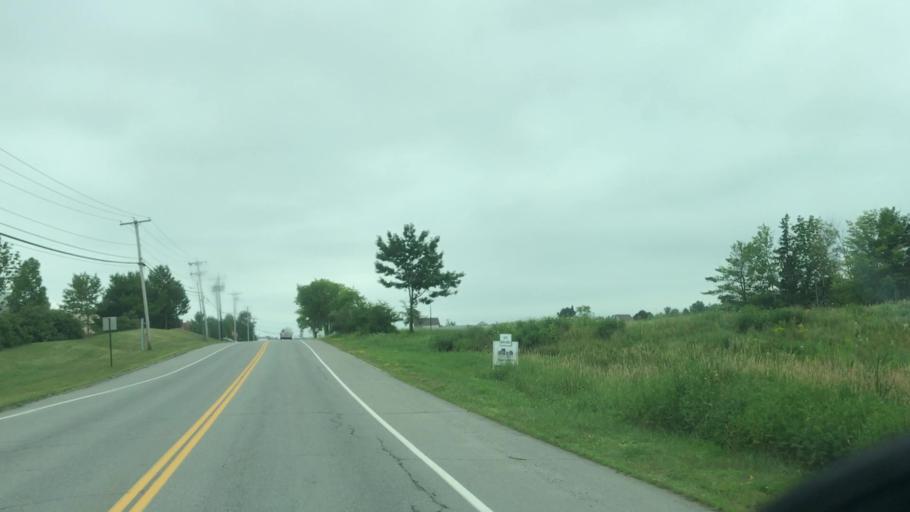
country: US
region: Maine
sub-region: Penobscot County
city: Veazie
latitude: 44.8445
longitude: -68.7414
